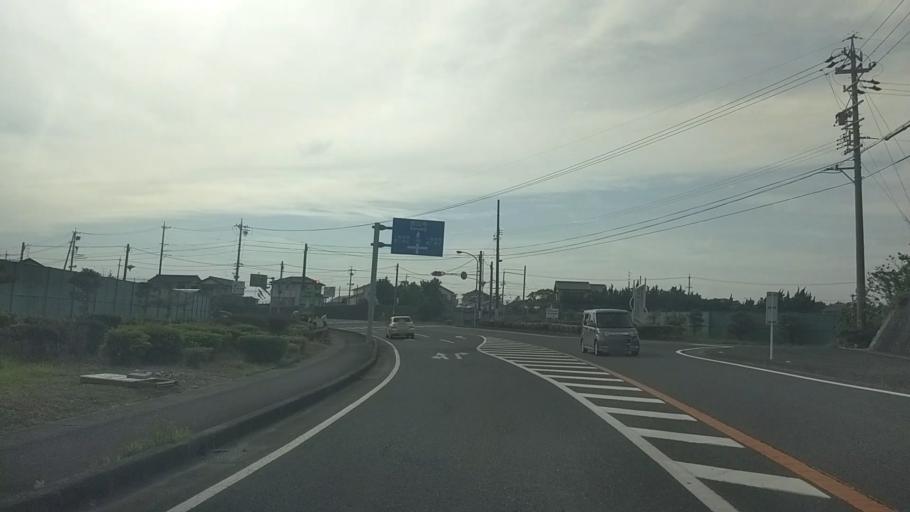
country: JP
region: Shizuoka
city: Hamamatsu
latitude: 34.7647
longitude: 137.6432
